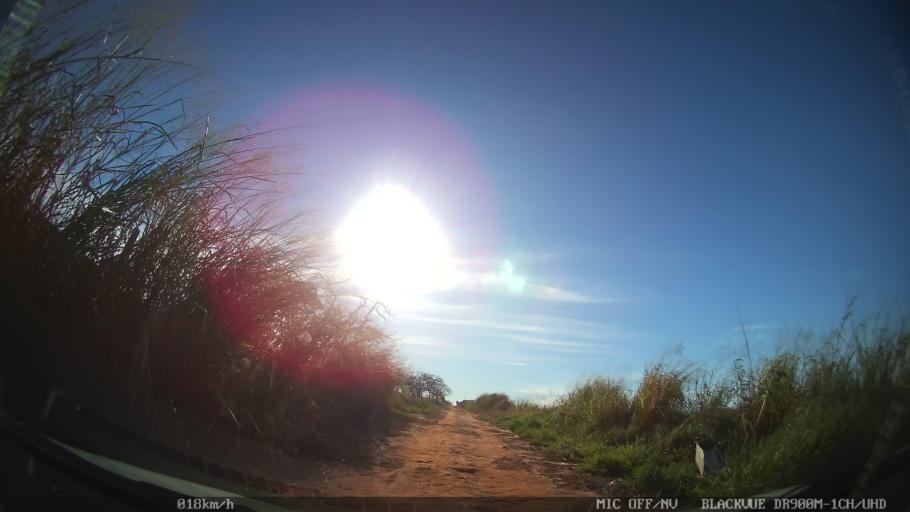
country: BR
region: Sao Paulo
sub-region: Sao Jose Do Rio Preto
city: Sao Jose do Rio Preto
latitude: -20.8798
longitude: -49.3173
